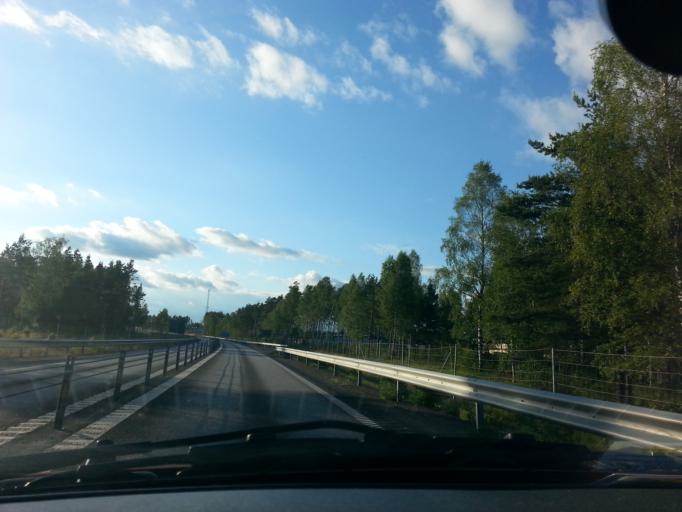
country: SE
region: Joenkoeping
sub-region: Gislaveds Kommun
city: Gislaved
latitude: 57.2764
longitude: 13.6154
